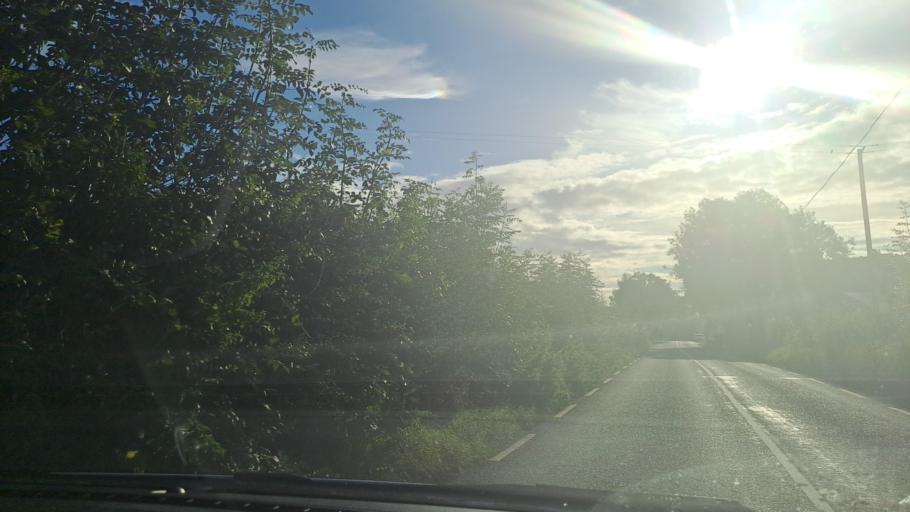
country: IE
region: Ulster
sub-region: County Monaghan
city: Carrickmacross
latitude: 53.9894
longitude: -6.7697
